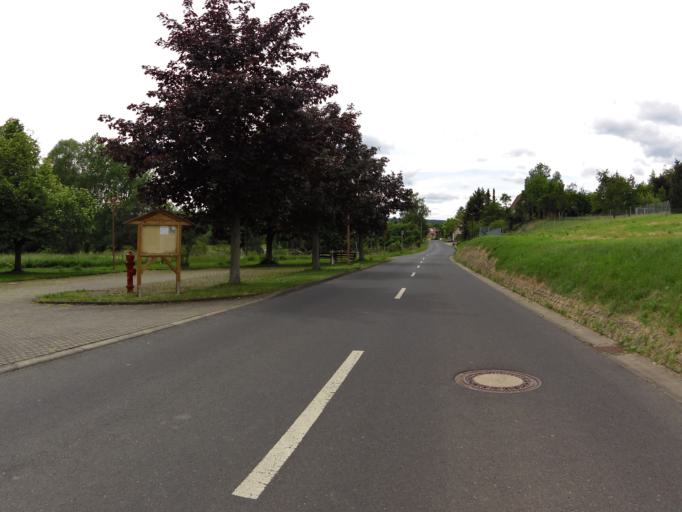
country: DE
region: Thuringia
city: Oberdorla
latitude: 51.1644
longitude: 10.4319
